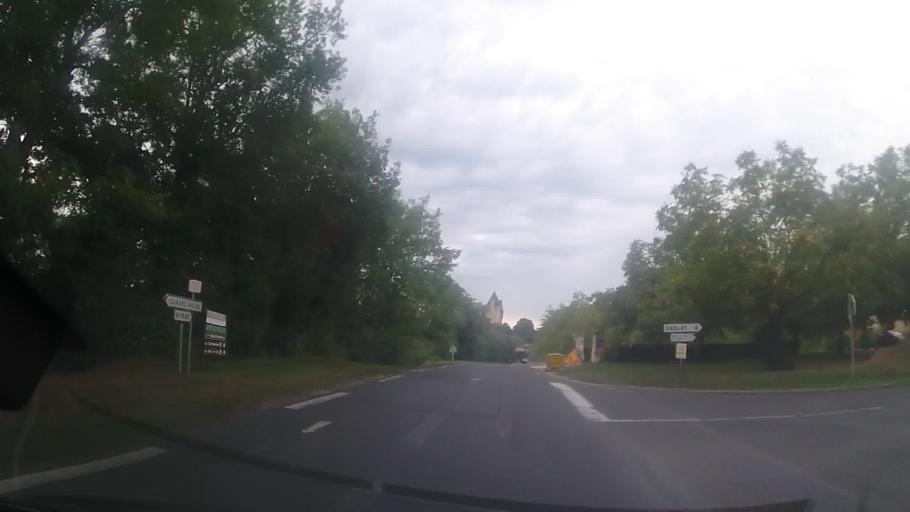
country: FR
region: Aquitaine
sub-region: Departement de la Dordogne
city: Carsac-Aillac
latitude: 44.8416
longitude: 1.2493
